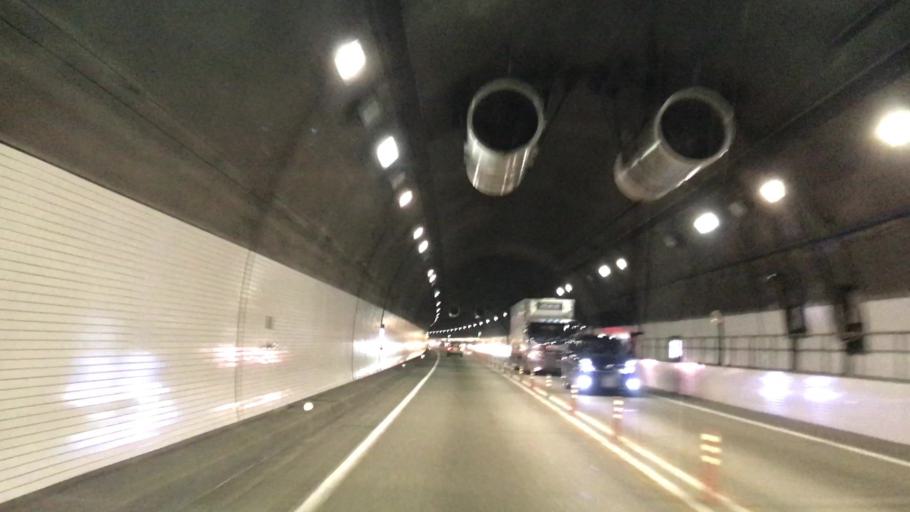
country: JP
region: Hokkaido
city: Iwamizawa
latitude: 42.9323
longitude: 142.1122
